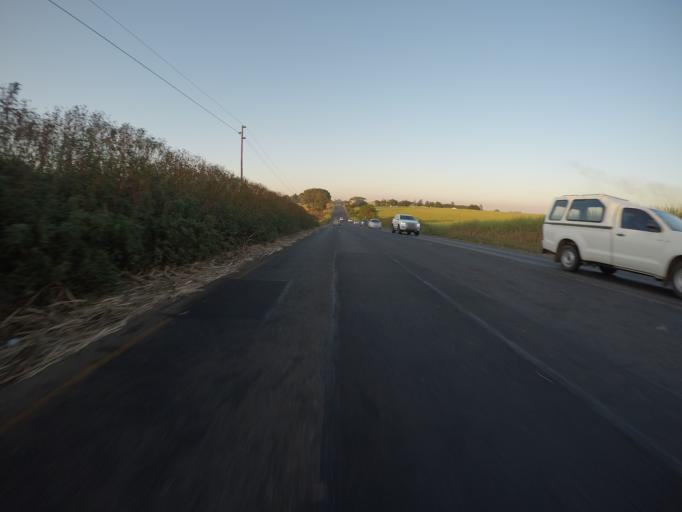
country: ZA
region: KwaZulu-Natal
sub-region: uThungulu District Municipality
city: Empangeni
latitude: -28.7858
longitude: 31.8973
